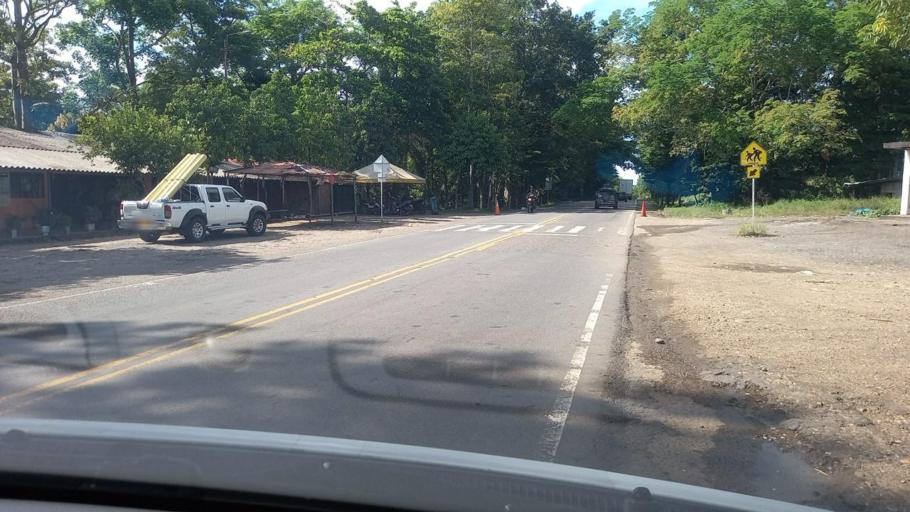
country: CO
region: Antioquia
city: Yondo
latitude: 6.8451
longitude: -73.7761
